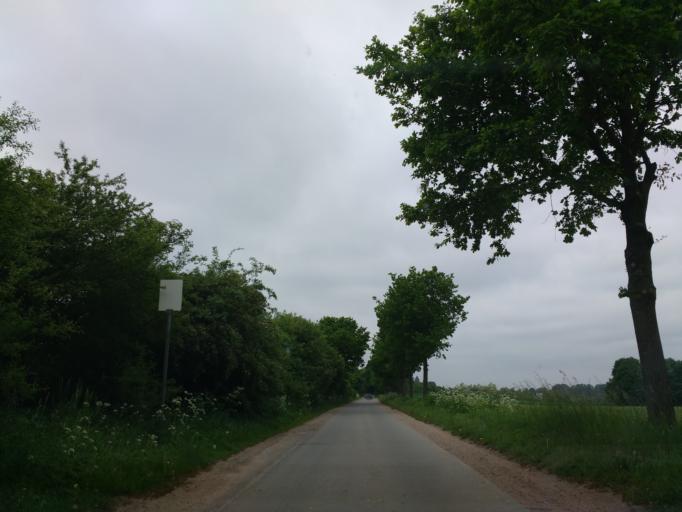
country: DE
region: Mecklenburg-Vorpommern
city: Zurow
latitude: 53.8627
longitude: 11.6325
